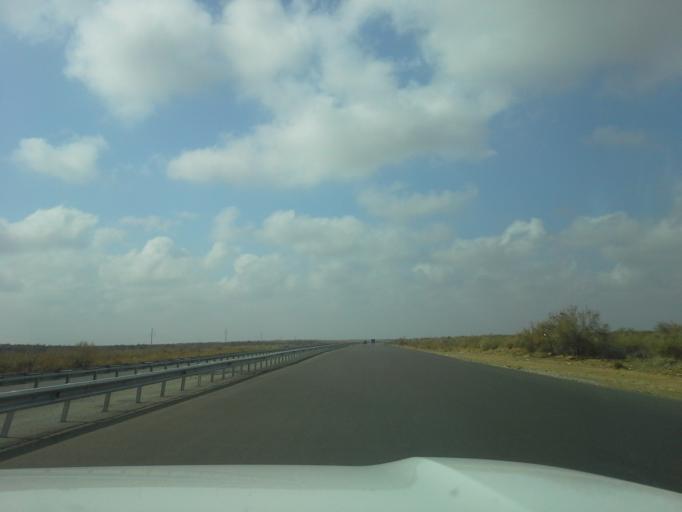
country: TM
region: Mary
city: Mary
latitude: 37.3914
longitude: 61.5049
